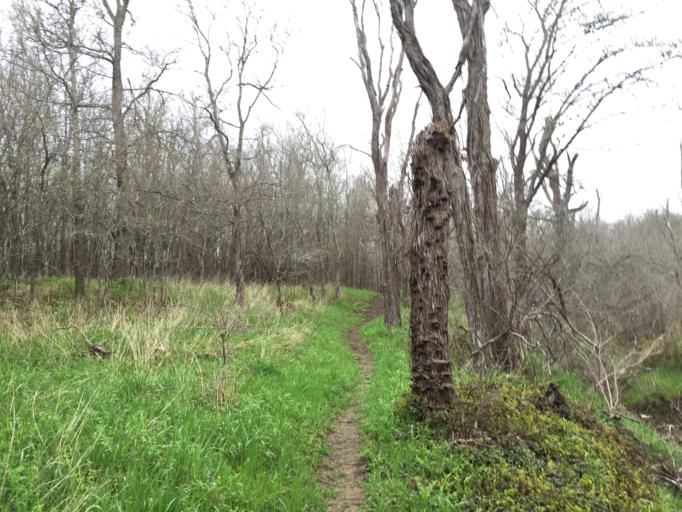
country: US
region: Texas
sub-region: Bastrop County
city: Bastrop
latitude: 30.0898
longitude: -97.3172
